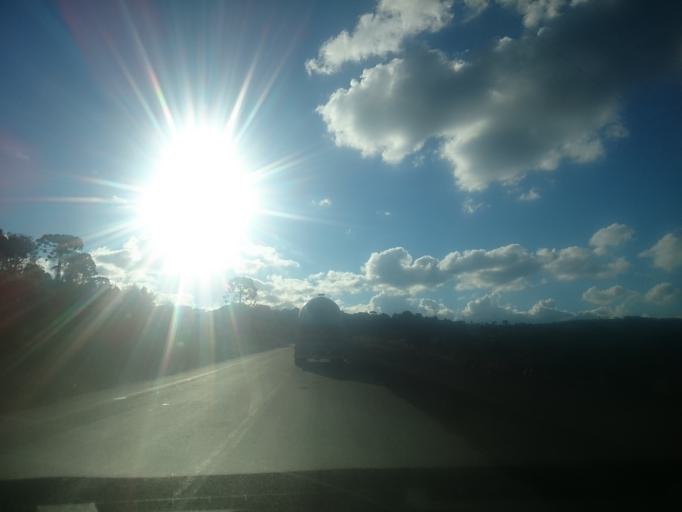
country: BR
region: Santa Catarina
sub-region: Sao Joaquim
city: Sao Joaquim
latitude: -28.0817
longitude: -50.0651
